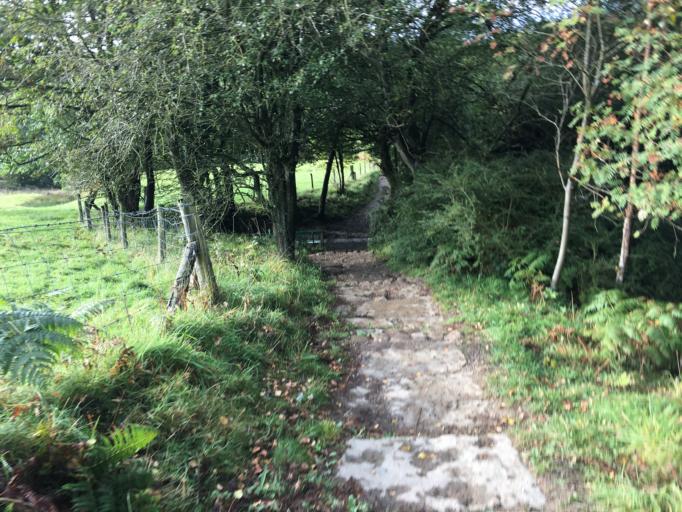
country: GB
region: England
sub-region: North Yorkshire
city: Sleights
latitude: 54.3977
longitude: -0.7285
